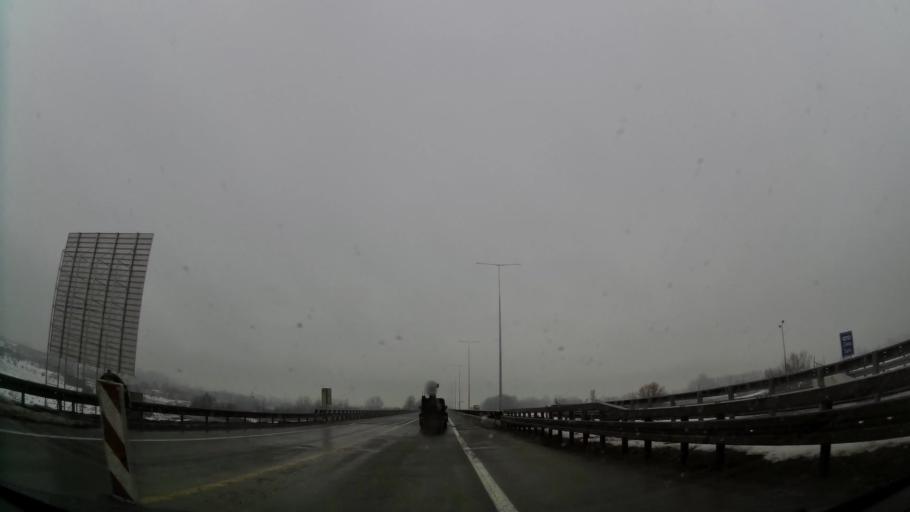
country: RS
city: Ostruznica
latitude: 44.7359
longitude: 20.3297
